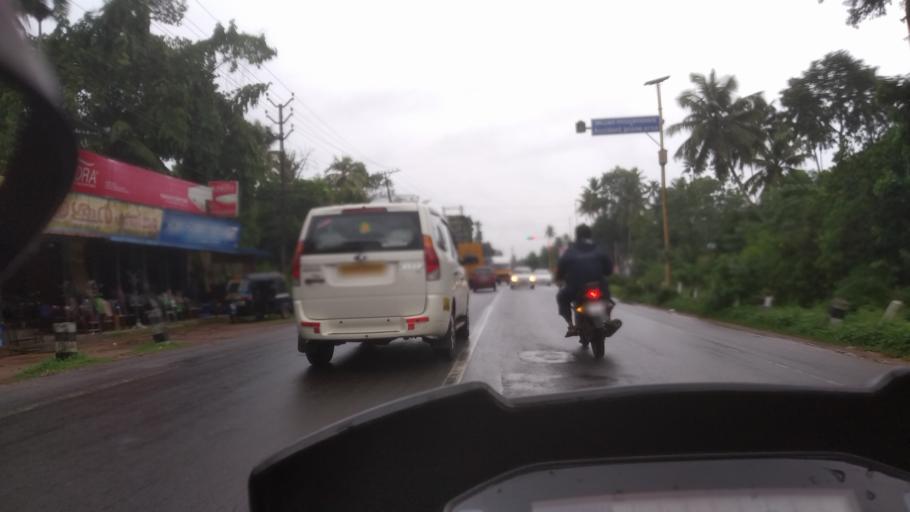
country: IN
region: Kerala
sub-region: Alappuzha
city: Kayankulam
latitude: 9.1292
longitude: 76.5154
